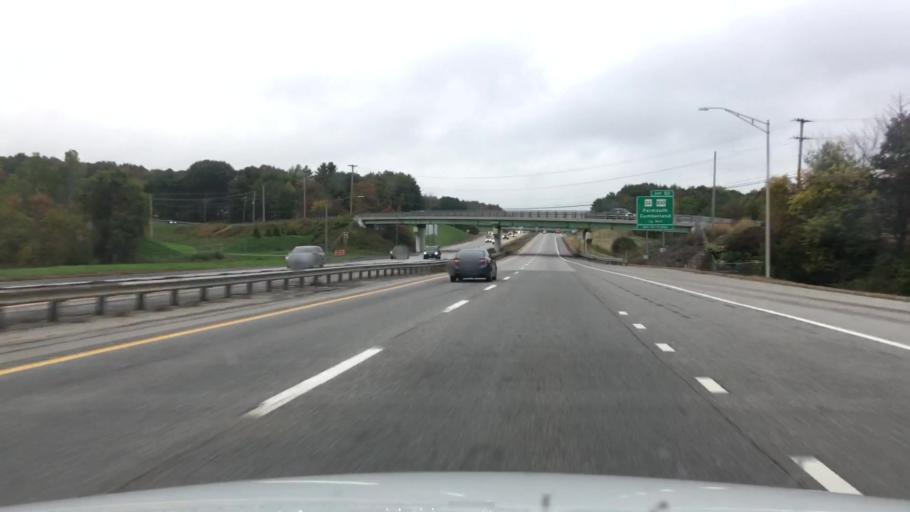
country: US
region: Maine
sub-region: Cumberland County
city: Falmouth
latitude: 43.7248
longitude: -70.3040
